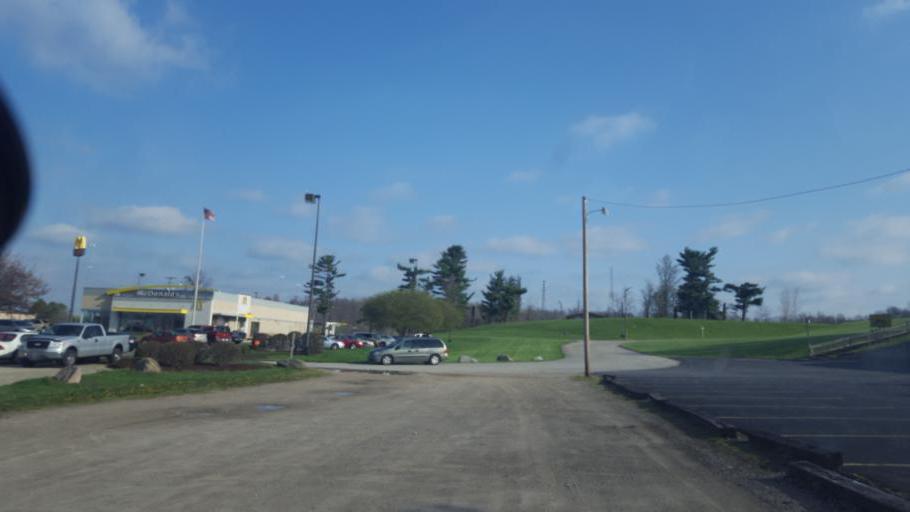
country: US
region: Ohio
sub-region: Sandusky County
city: Bellville
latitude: 40.6478
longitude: -82.5420
